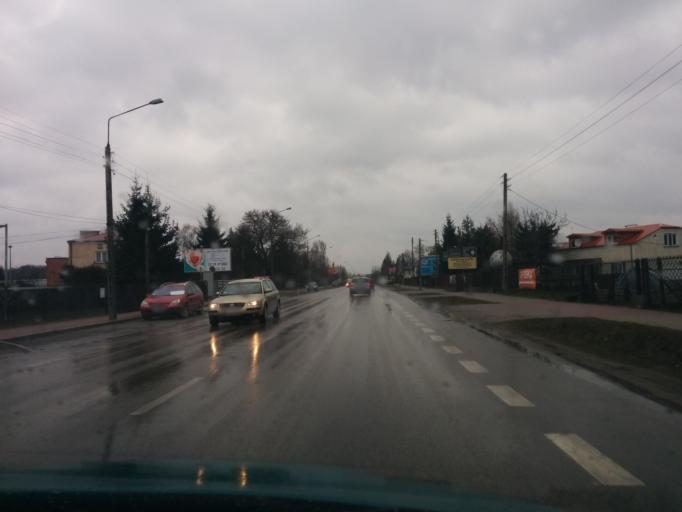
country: PL
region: Masovian Voivodeship
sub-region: Powiat legionowski
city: Jablonna
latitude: 52.3707
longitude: 20.9286
